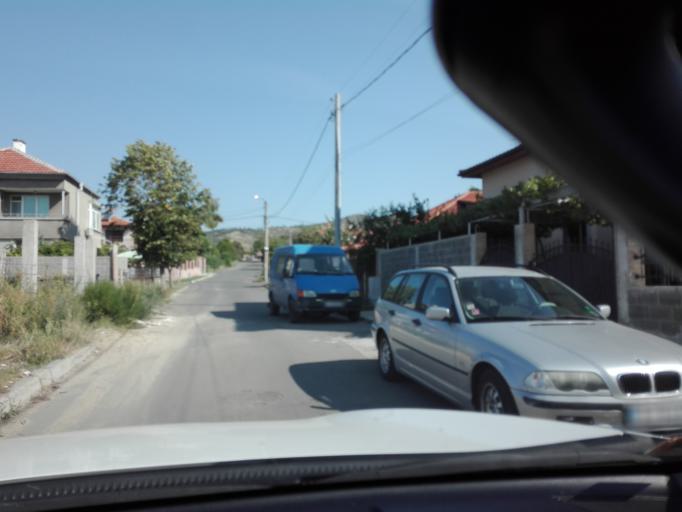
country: BG
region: Burgas
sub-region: Obshtina Kameno
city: Kameno
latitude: 42.6257
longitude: 27.3923
